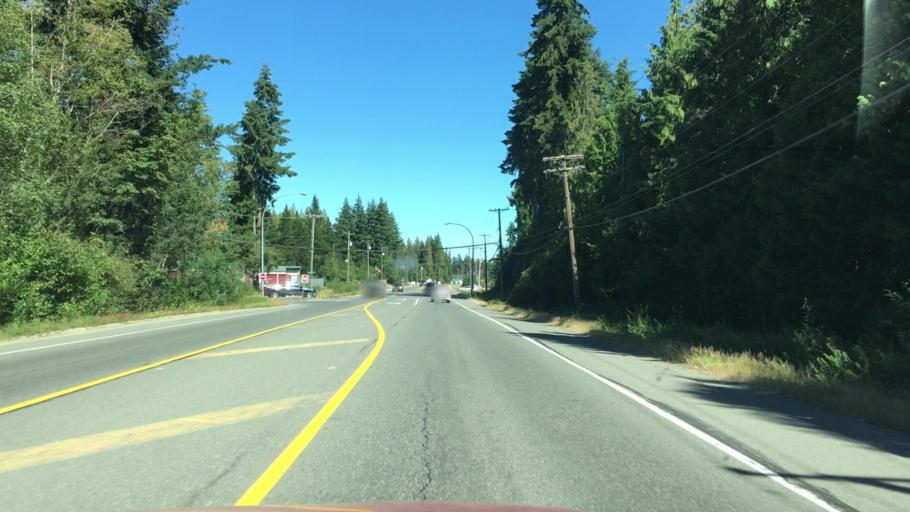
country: CA
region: British Columbia
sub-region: Regional District of Nanaimo
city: Parksville
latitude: 49.3064
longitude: -124.4845
